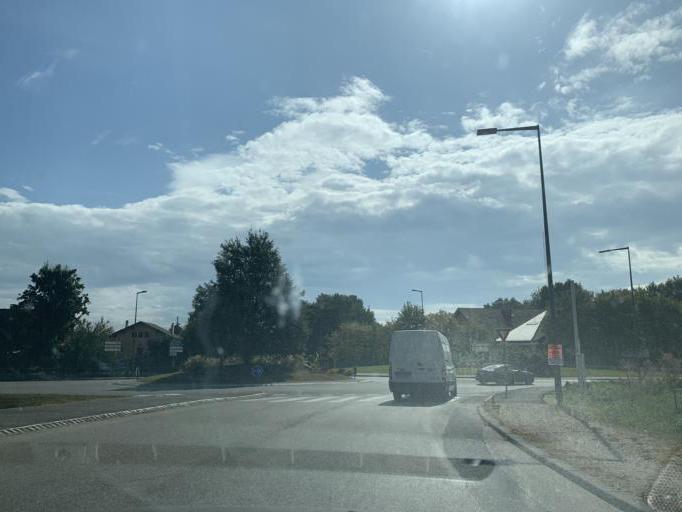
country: FR
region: Rhone-Alpes
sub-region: Departement de l'Ain
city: Divonne-les-Bains
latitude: 46.3486
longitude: 6.1365
